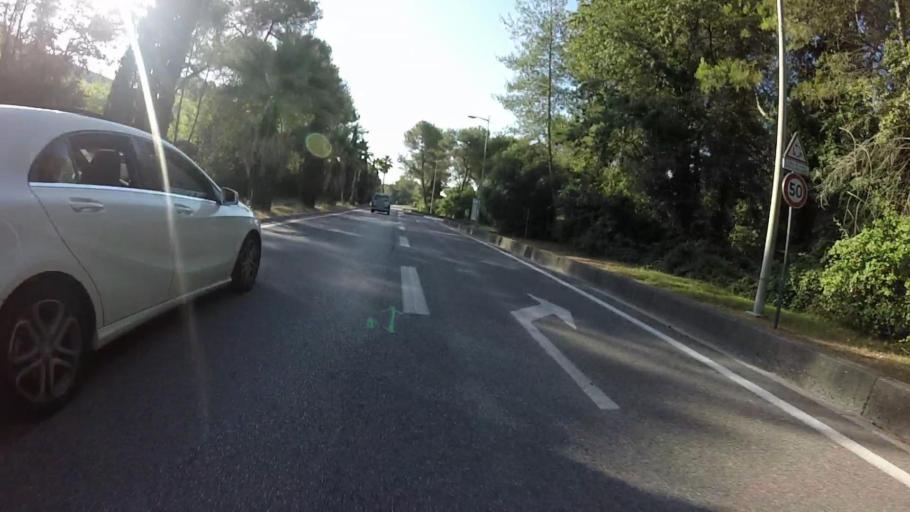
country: FR
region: Provence-Alpes-Cote d'Azur
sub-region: Departement des Alpes-Maritimes
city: Mougins
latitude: 43.6120
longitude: 7.0160
